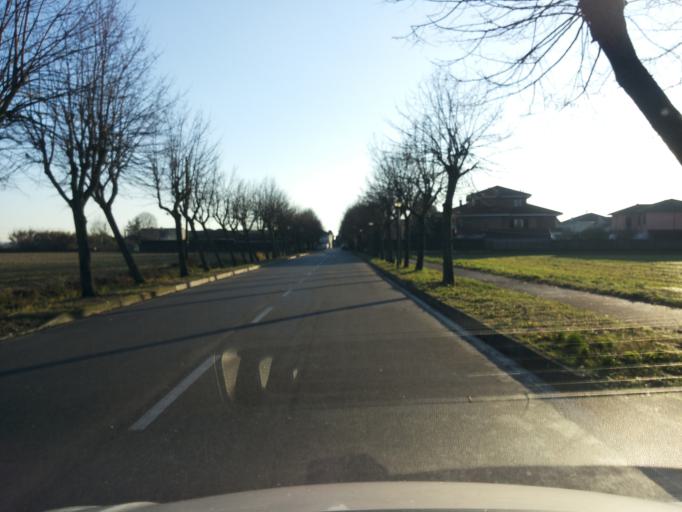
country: IT
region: Piedmont
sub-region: Provincia di Vercelli
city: Lignana
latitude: 45.2886
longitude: 8.3475
